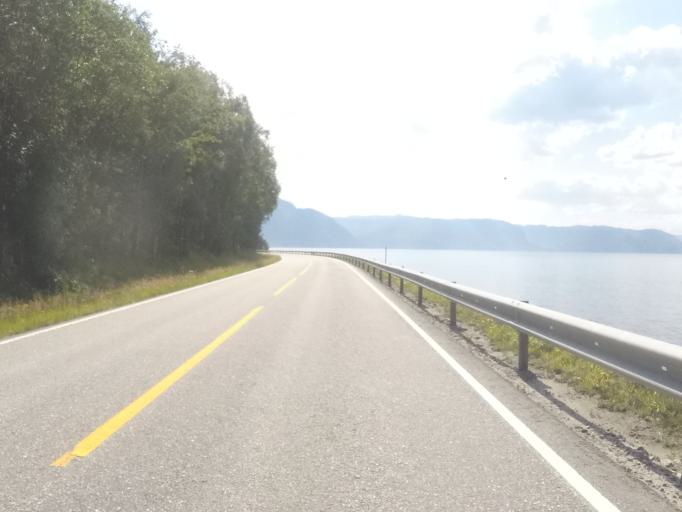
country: NO
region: Sogn og Fjordane
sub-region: Gaular
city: Sande
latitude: 61.1490
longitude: 5.6246
